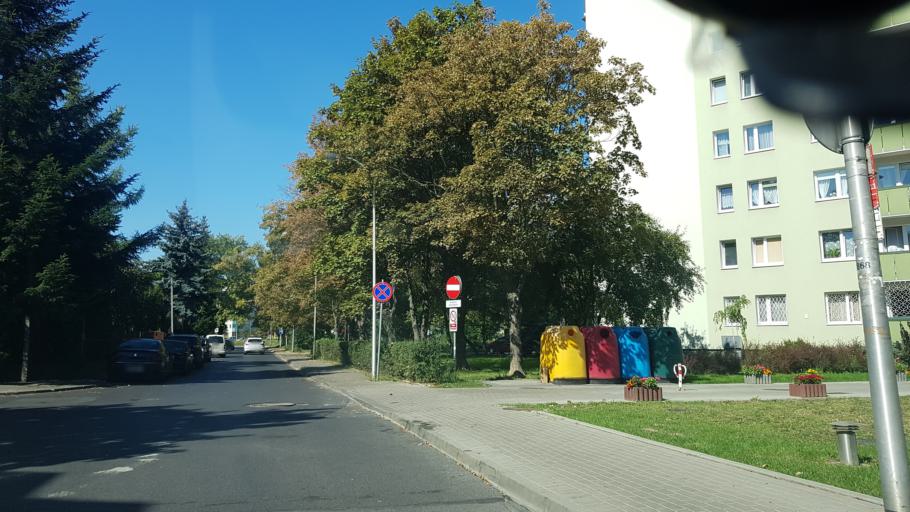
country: PL
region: Masovian Voivodeship
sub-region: Warszawa
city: Mokotow
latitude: 52.1784
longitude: 21.0197
